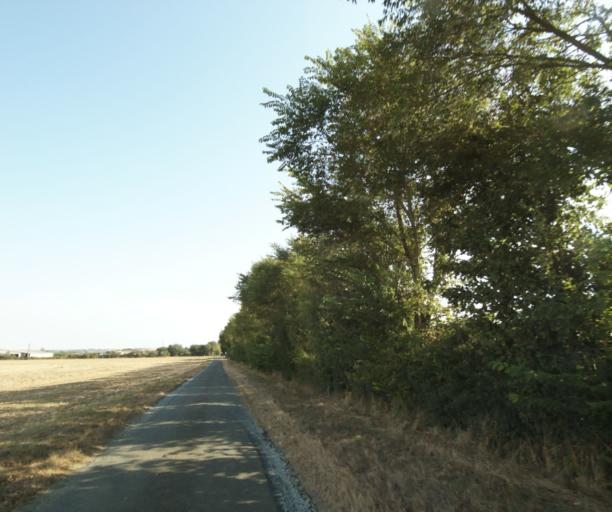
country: FR
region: Poitou-Charentes
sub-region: Departement de la Charente-Maritime
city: Muron
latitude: 45.9819
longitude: -0.8236
